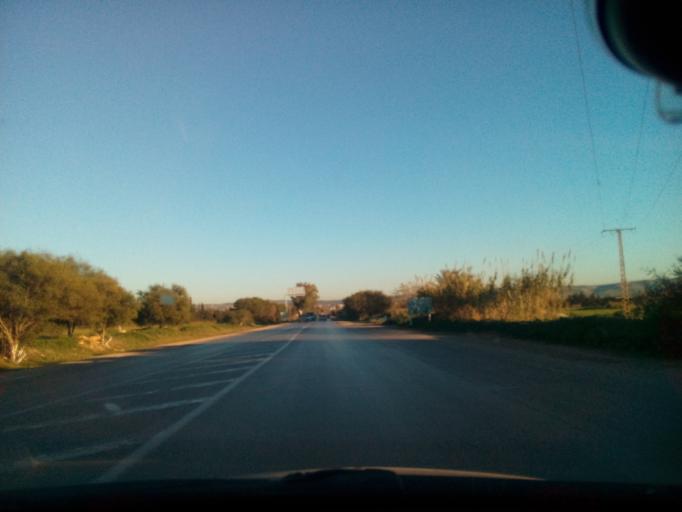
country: DZ
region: Mostaganem
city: Mostaganem
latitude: 35.7586
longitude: 0.2232
